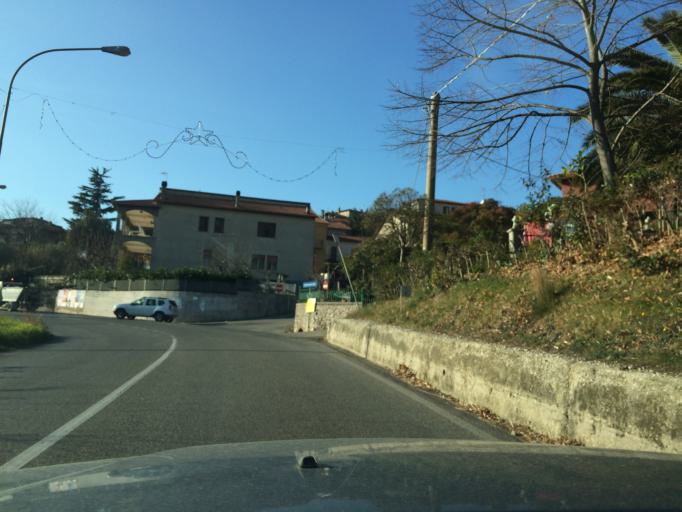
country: IT
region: Umbria
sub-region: Provincia di Terni
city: Fornole
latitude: 42.5432
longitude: 12.4589
